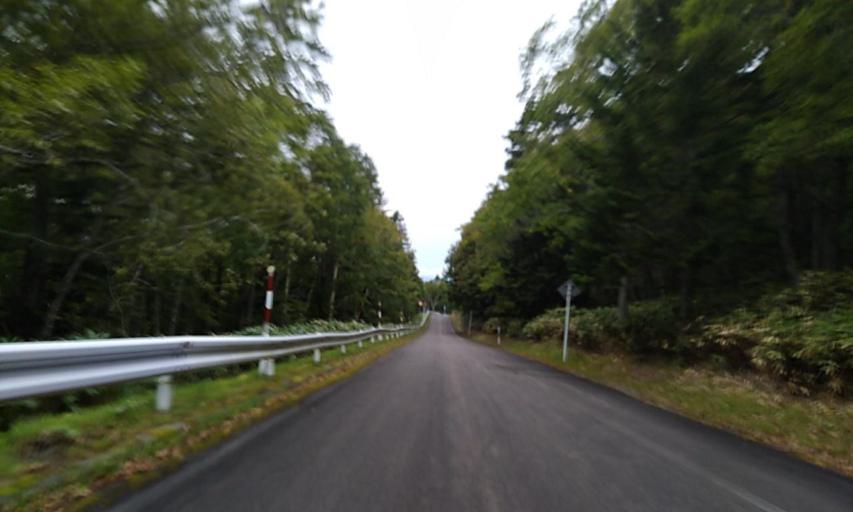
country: JP
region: Hokkaido
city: Bihoro
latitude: 43.5657
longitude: 144.2109
